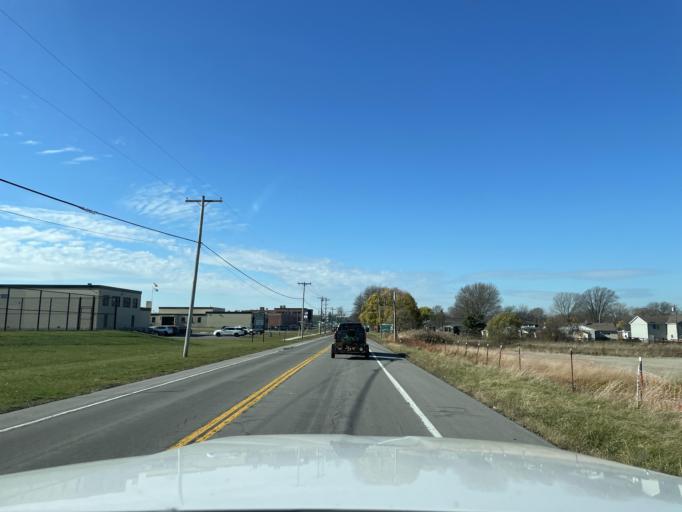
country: US
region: New York
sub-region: Niagara County
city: Middleport
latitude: 43.2131
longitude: -78.4641
